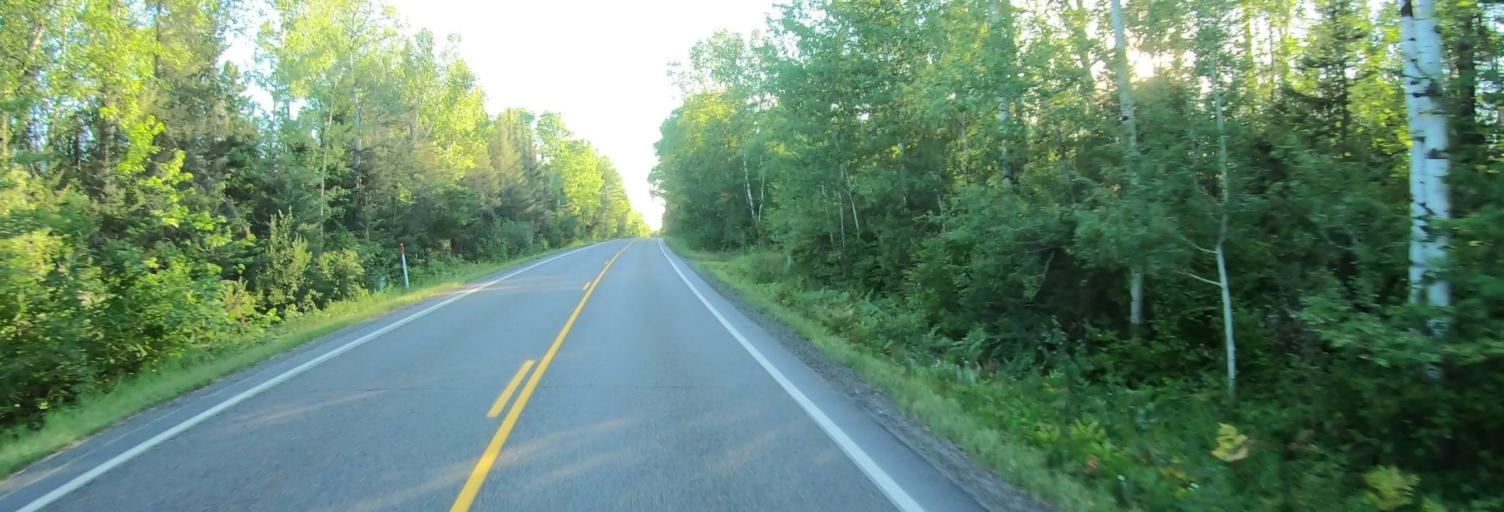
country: US
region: Minnesota
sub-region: Saint Louis County
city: Ely
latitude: 47.9443
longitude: -91.6638
